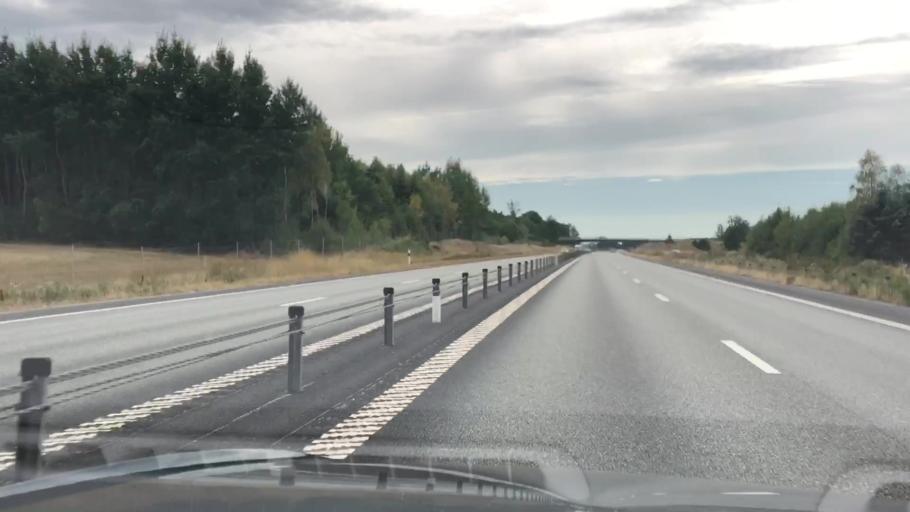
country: SE
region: Blekinge
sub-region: Karlshamns Kommun
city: Morrum
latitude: 56.1440
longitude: 14.6629
